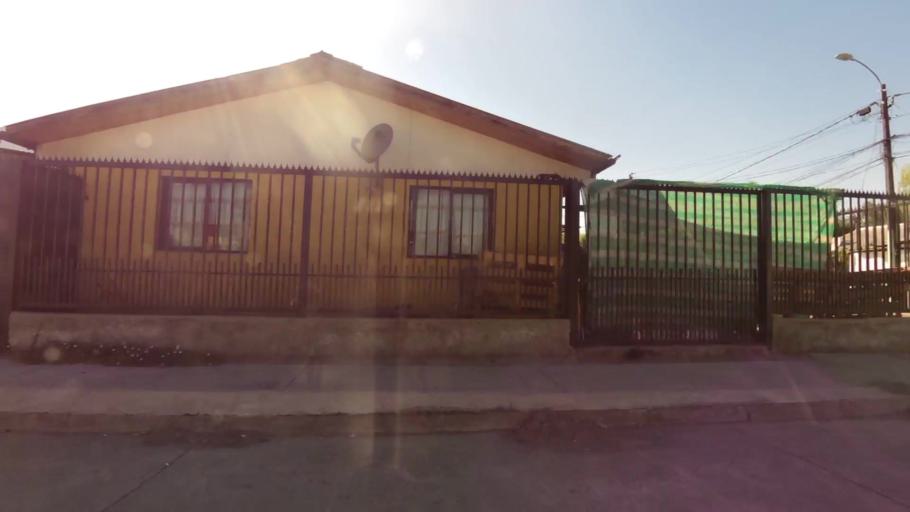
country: CL
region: Maule
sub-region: Provincia de Curico
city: Curico
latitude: -34.9992
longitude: -71.2490
